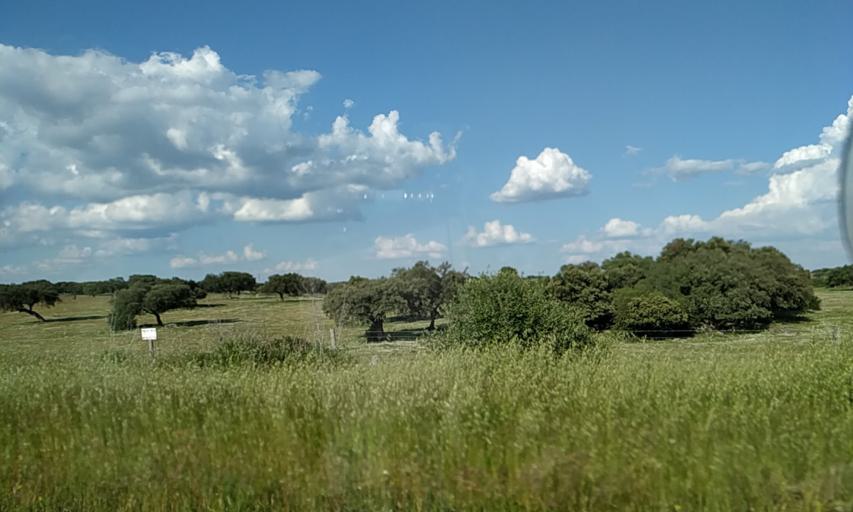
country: PT
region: Portalegre
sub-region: Portalegre
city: Urra
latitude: 39.1374
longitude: -7.4498
